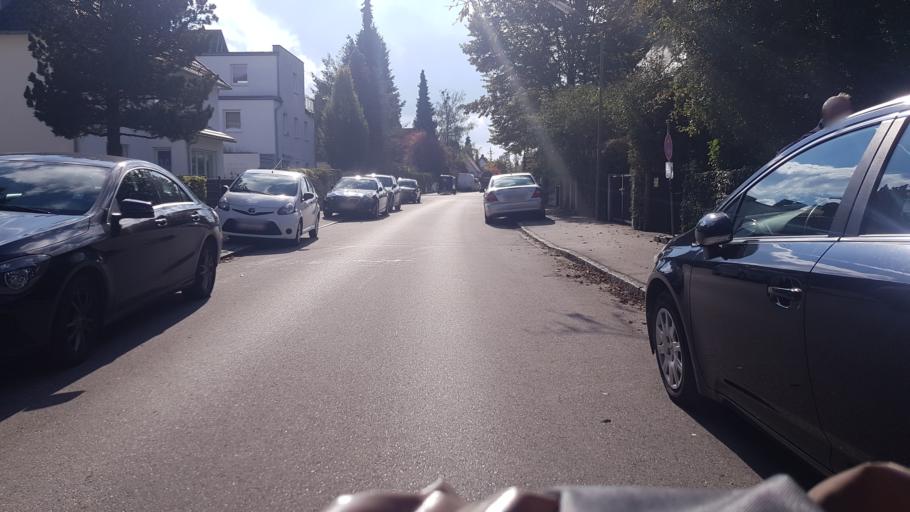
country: DE
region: Bavaria
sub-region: Upper Bavaria
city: Pasing
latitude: 48.1343
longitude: 11.4906
